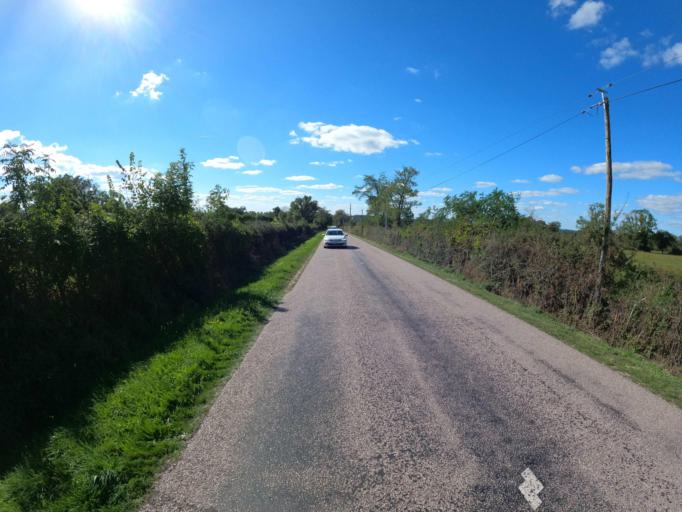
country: FR
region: Auvergne
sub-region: Departement de l'Allier
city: Buxieres-les-Mines
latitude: 46.4042
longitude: 3.0091
